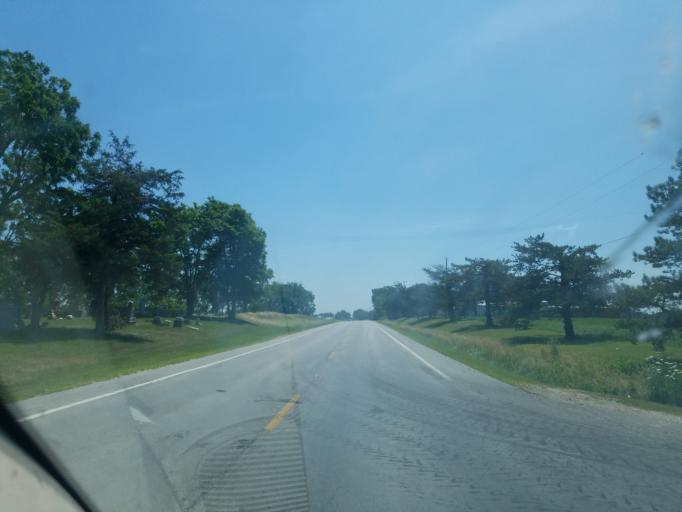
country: US
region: Ohio
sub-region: Mercer County
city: Rockford
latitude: 40.7280
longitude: -84.7420
